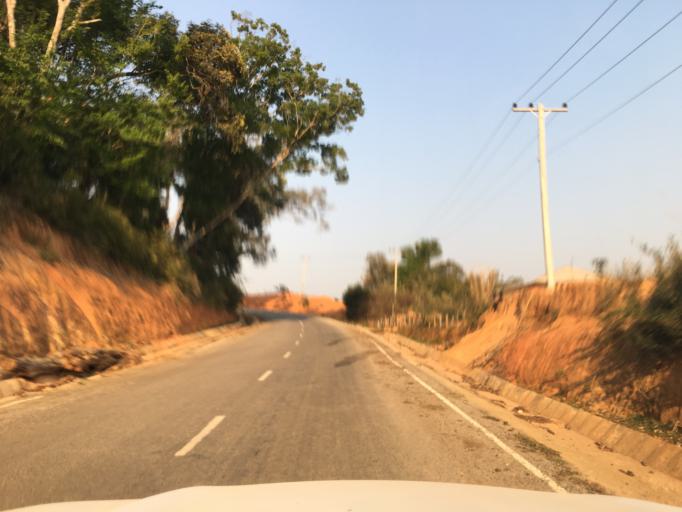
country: LA
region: Houaphan
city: Xam Nua
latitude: 20.6036
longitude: 104.0720
